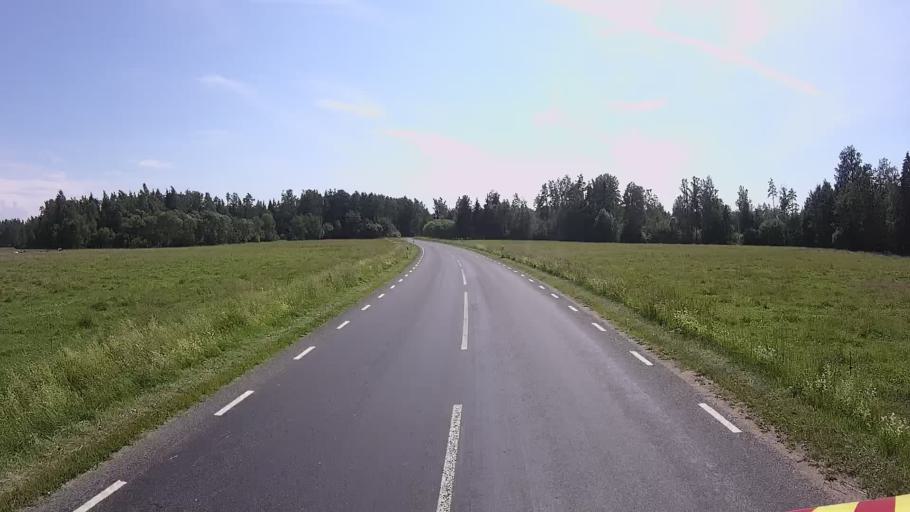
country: EE
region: Viljandimaa
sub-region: Karksi vald
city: Karksi-Nuia
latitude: 58.0563
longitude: 25.5485
